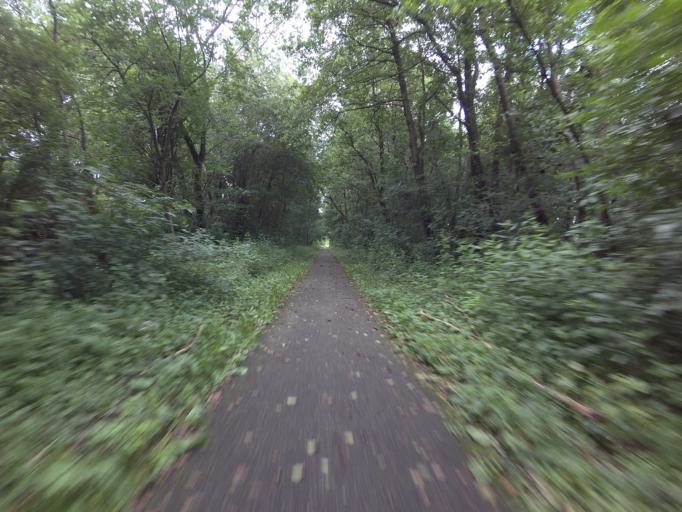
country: DK
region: Central Jutland
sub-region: Favrskov Kommune
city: Hammel
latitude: 56.3169
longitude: 9.8677
